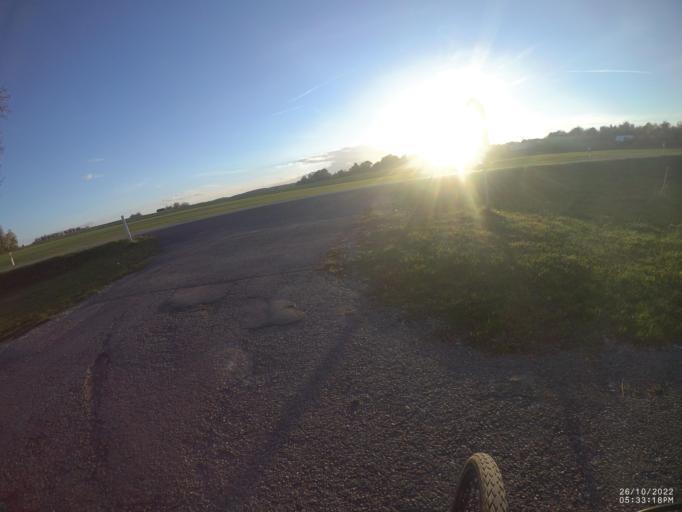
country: DE
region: Baden-Wuerttemberg
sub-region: Regierungsbezirk Stuttgart
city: Hohenstadt
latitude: 48.5406
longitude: 9.6825
